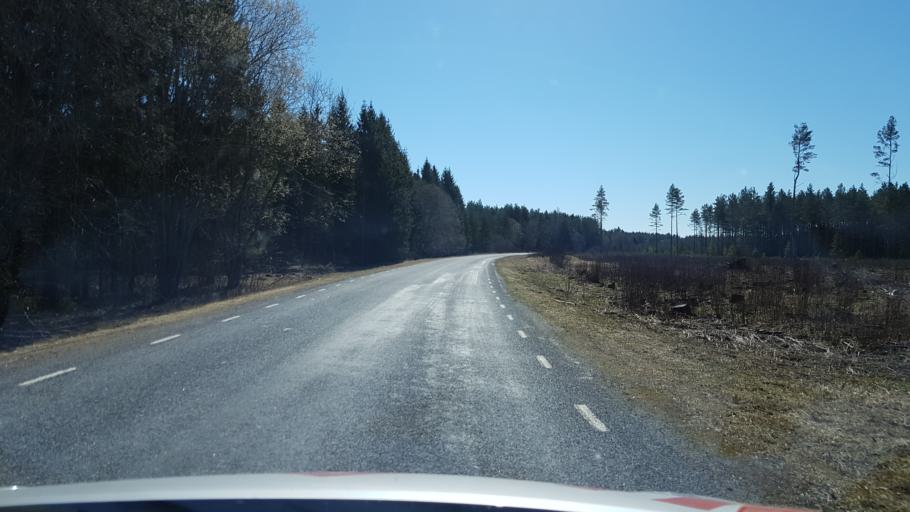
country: EE
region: Laeaene-Virumaa
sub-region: Haljala vald
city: Haljala
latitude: 59.5086
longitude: 26.2360
